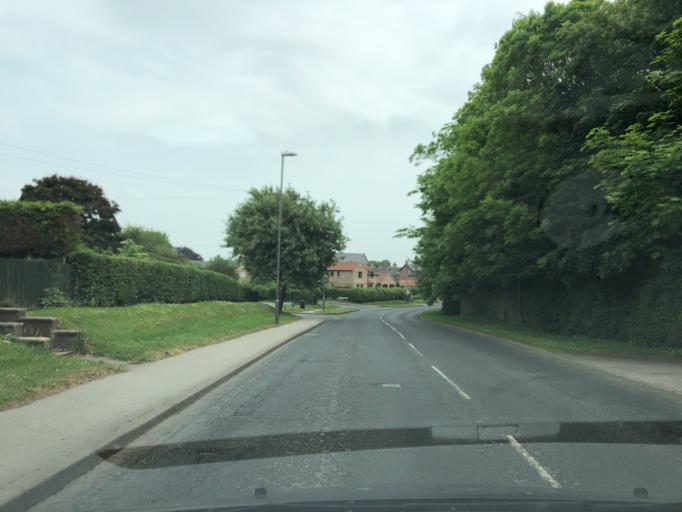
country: GB
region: England
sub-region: North Yorkshire
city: Boroughbridge
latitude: 54.0930
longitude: -1.4010
